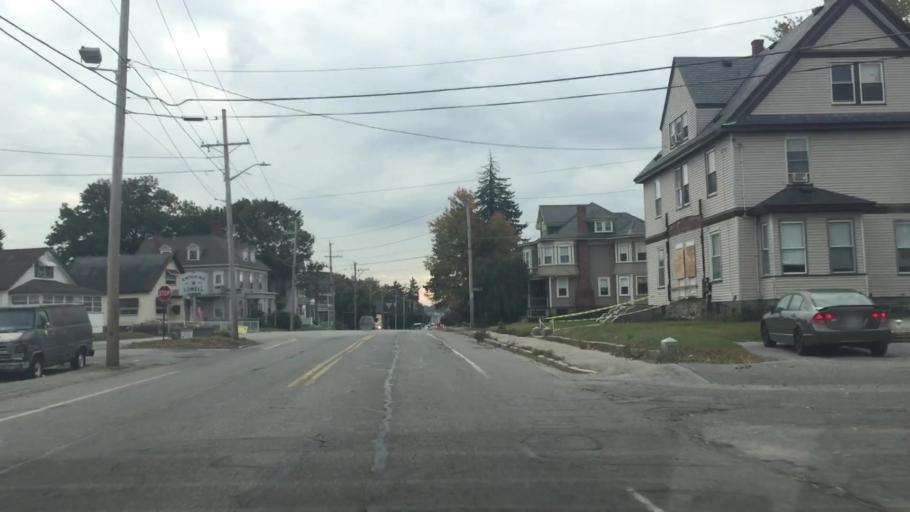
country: US
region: Massachusetts
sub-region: Middlesex County
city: Dracut
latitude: 42.6626
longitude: -71.3194
